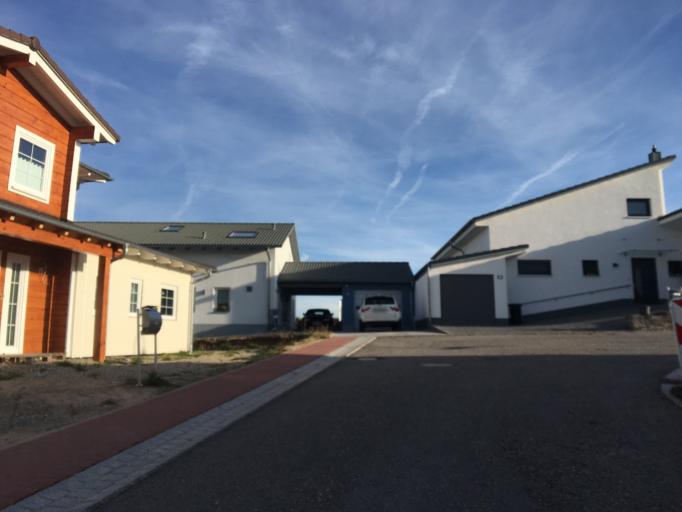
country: DE
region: Bavaria
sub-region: Regierungsbezirk Mittelfranken
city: Wilhermsdorf
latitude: 49.4740
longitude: 10.7256
